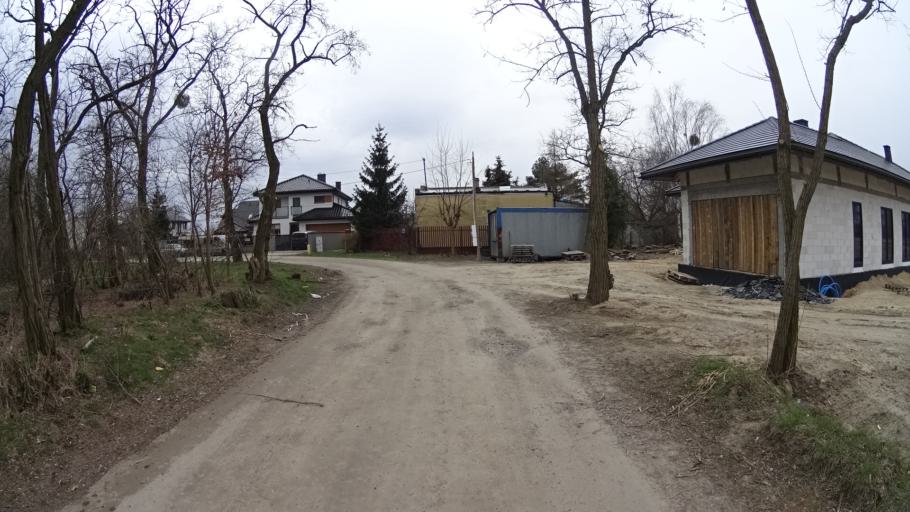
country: PL
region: Masovian Voivodeship
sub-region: Powiat warszawski zachodni
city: Ozarow Mazowiecki
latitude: 52.2319
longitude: 20.7899
